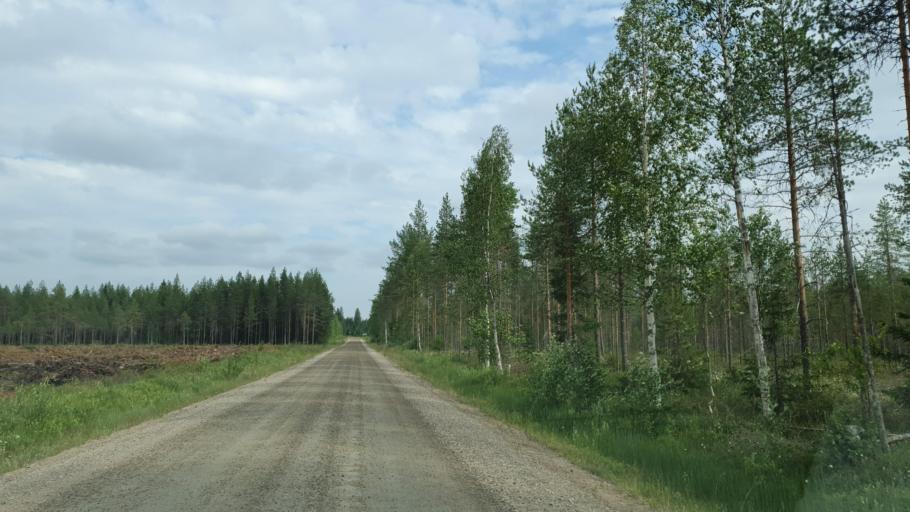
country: FI
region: Kainuu
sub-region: Kehys-Kainuu
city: Kuhmo
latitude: 63.9117
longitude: 29.5240
